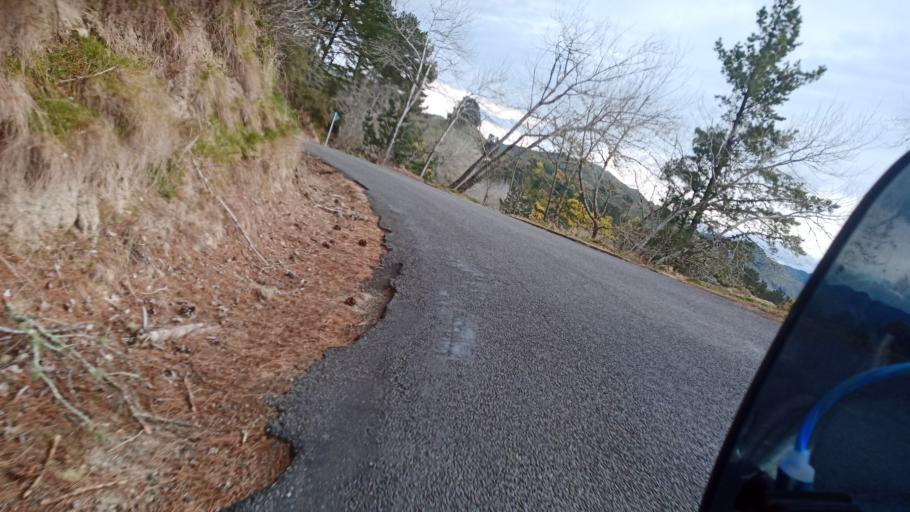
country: NZ
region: Hawke's Bay
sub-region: Wairoa District
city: Wairoa
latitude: -38.7731
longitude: 177.4210
